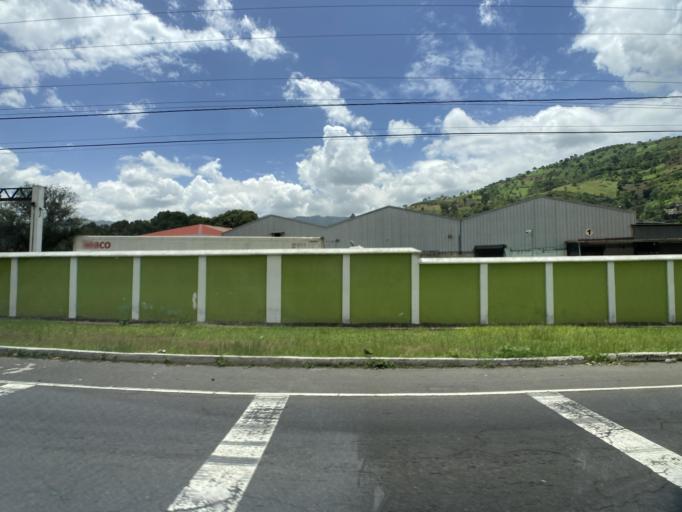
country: GT
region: Sacatepequez
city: San Antonio Aguas Calientes
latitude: 14.5355
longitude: -90.7704
